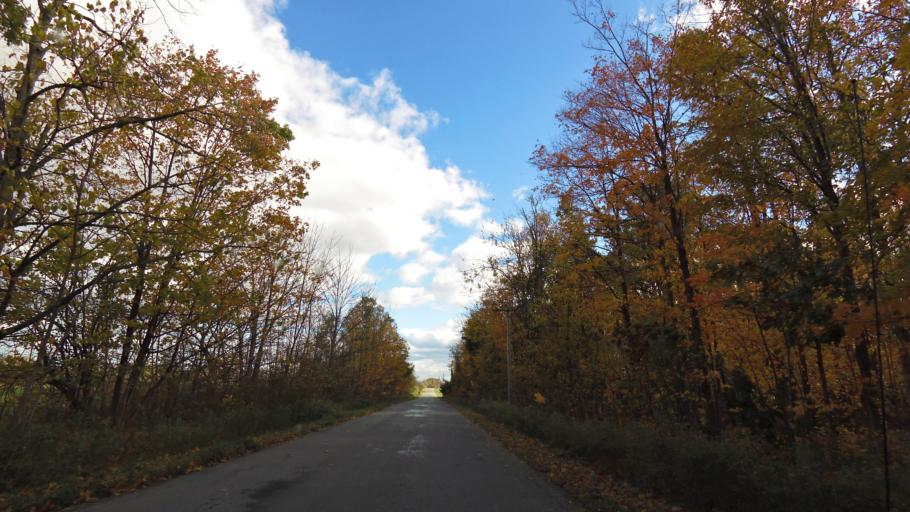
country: CA
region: Ontario
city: Burlington
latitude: 43.4452
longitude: -79.8497
